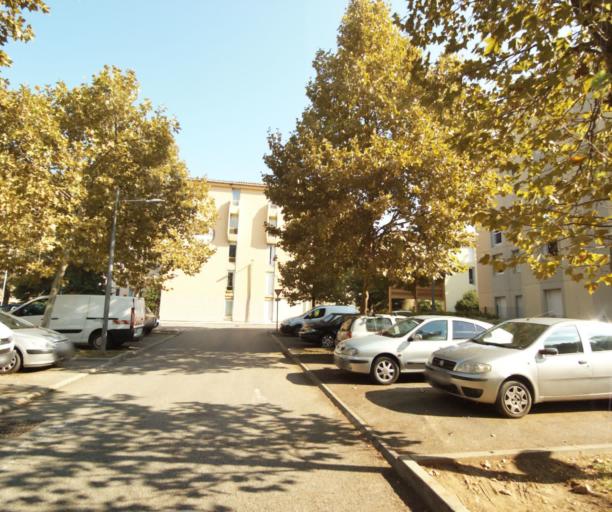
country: FR
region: Provence-Alpes-Cote d'Azur
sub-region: Departement des Alpes-Maritimes
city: Cantaron
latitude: 43.7702
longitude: 7.3318
